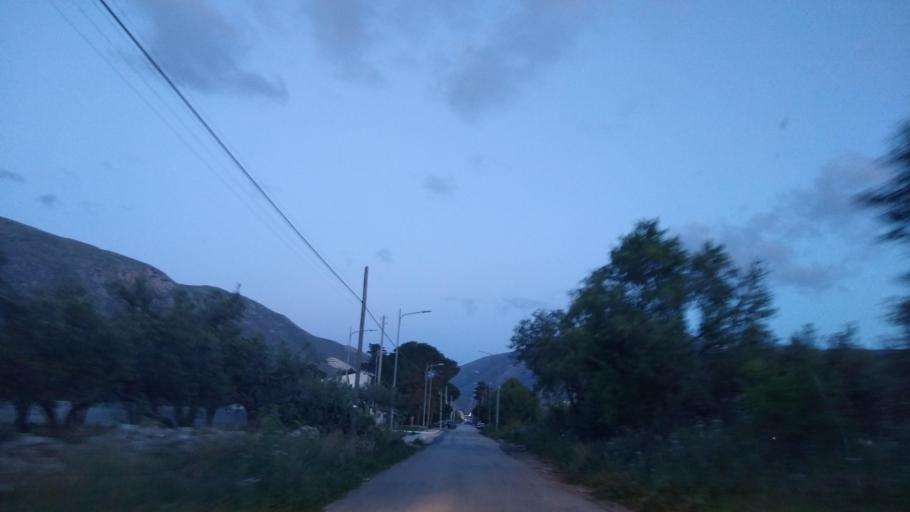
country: IT
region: Sicily
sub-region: Trapani
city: Castelluzzo
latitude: 38.1056
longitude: 12.7305
